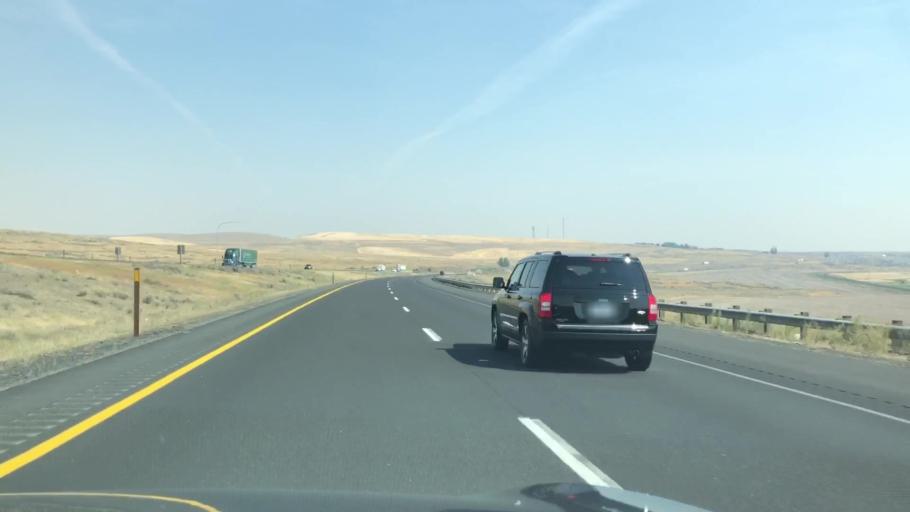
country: US
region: Washington
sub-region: Lincoln County
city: Davenport
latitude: 47.2947
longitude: -118.0283
